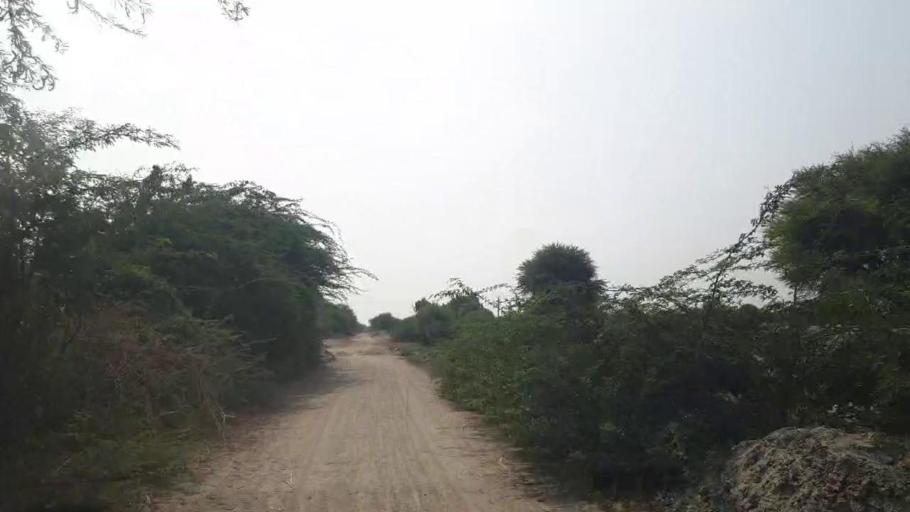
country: PK
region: Sindh
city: Badin
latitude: 24.6077
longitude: 68.7205
